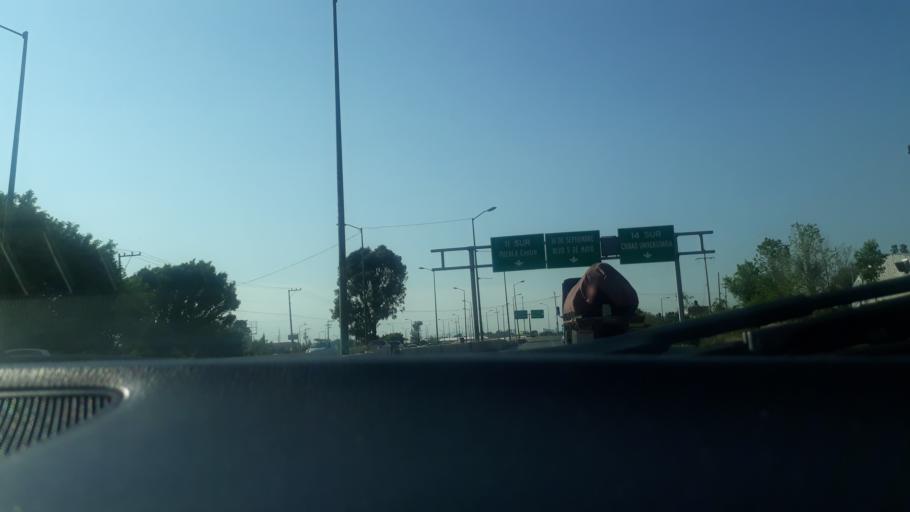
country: MX
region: Puebla
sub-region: Puebla
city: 18 de Marzo
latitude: 18.9765
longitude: -98.2125
